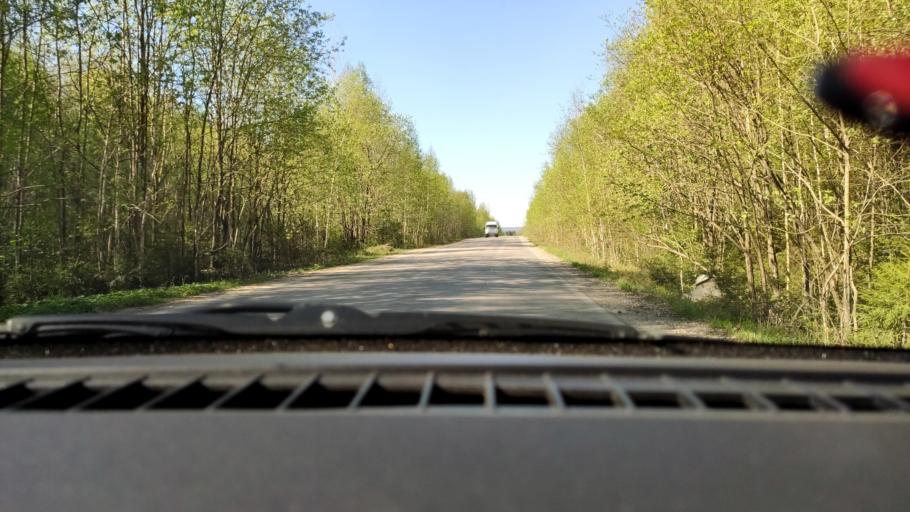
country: RU
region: Perm
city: Kondratovo
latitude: 58.0633
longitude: 56.0024
